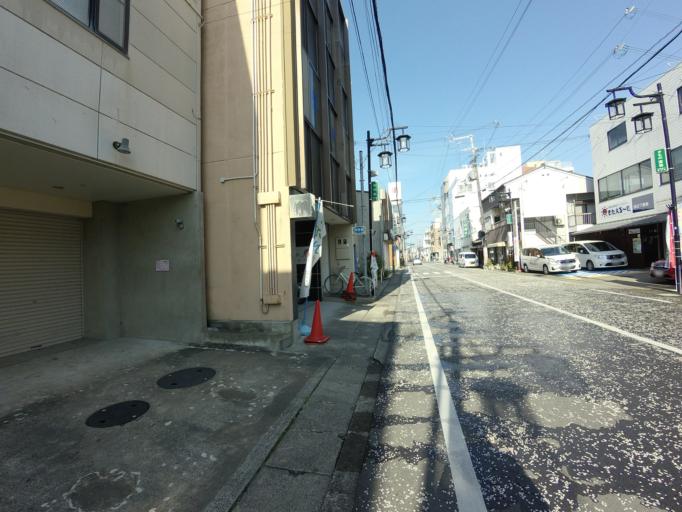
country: JP
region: Wakayama
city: Tanabe
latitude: 33.7302
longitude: 135.3823
